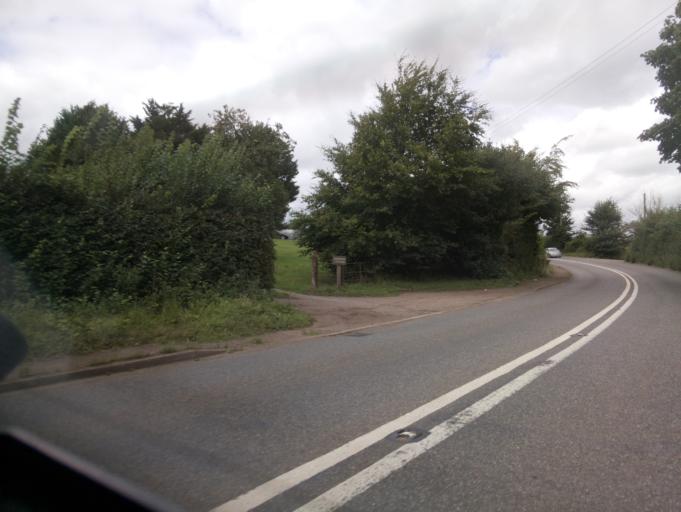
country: GB
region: England
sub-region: Devon
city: Bradninch
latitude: 50.7838
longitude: -3.4415
